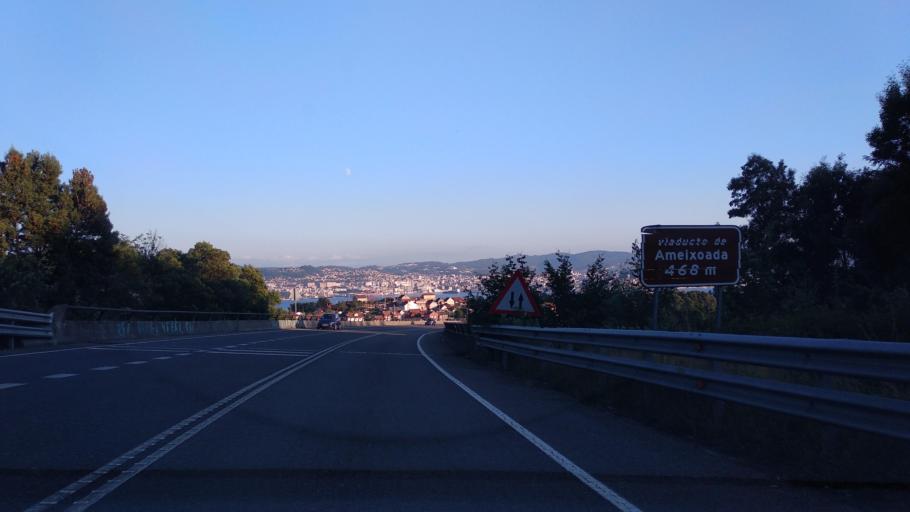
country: ES
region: Galicia
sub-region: Provincia de Pontevedra
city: Moana
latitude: 42.2841
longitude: -8.7538
